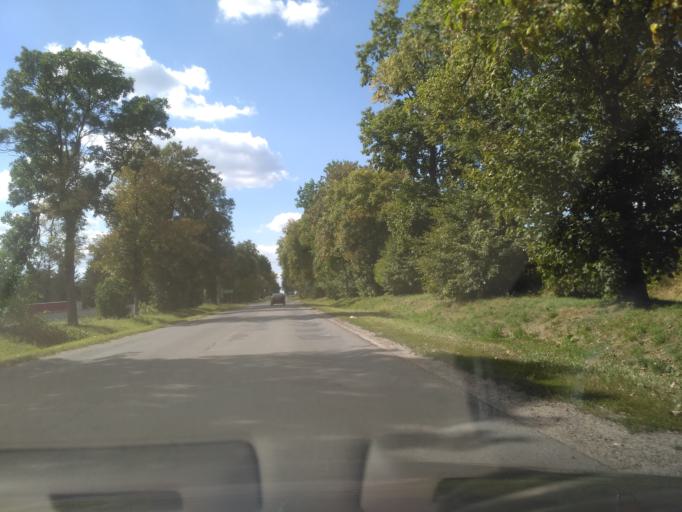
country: PL
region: Lublin Voivodeship
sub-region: Powiat swidnicki
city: Swidnik
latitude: 51.2135
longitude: 22.6405
